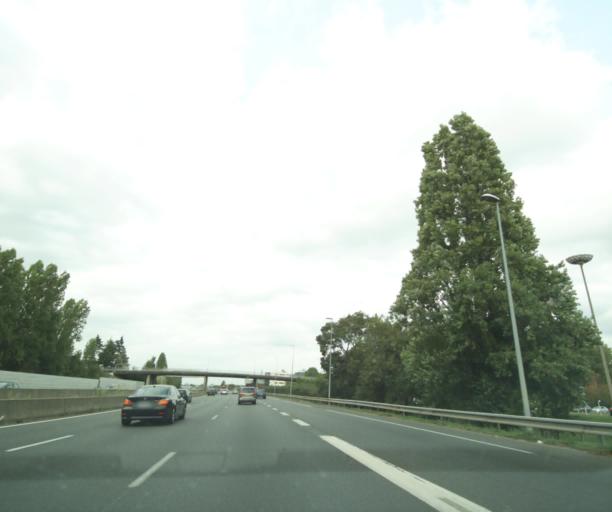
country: FR
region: Centre
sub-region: Departement d'Indre-et-Loire
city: Saint-Avertin
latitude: 47.3679
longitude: 0.7151
